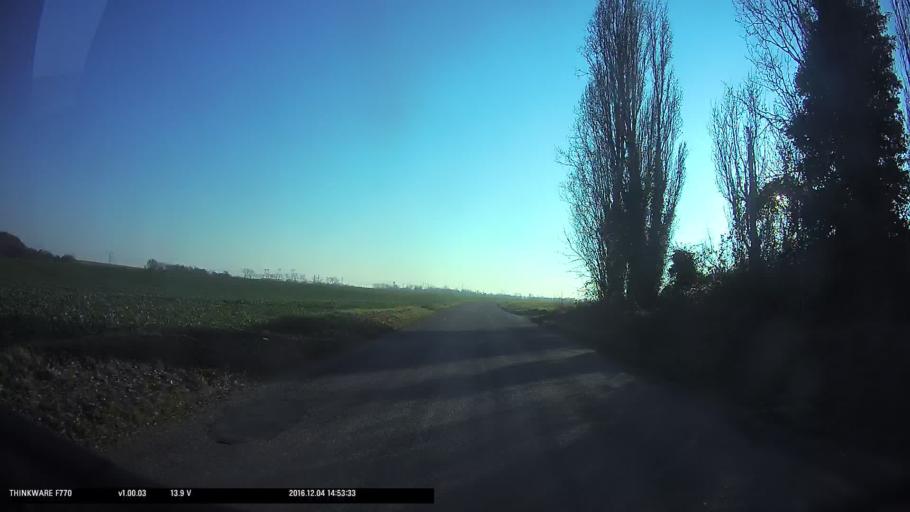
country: FR
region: Ile-de-France
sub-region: Departement du Val-d'Oise
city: Ableiges
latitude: 49.0695
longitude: 2.0049
